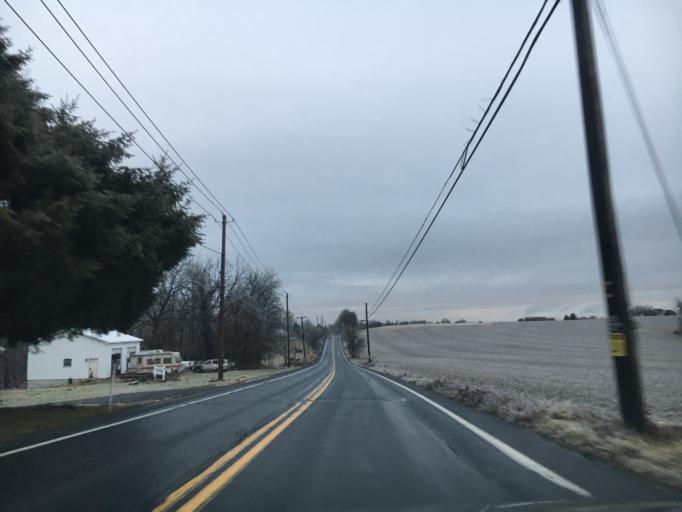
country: US
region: Pennsylvania
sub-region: Lehigh County
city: Schnecksville
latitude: 40.6224
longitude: -75.6290
